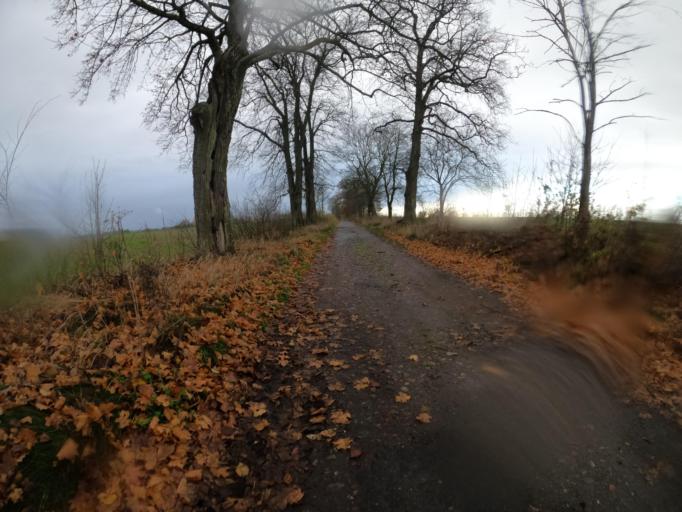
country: PL
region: West Pomeranian Voivodeship
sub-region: Powiat walecki
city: Tuczno
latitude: 53.2086
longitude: 16.2195
